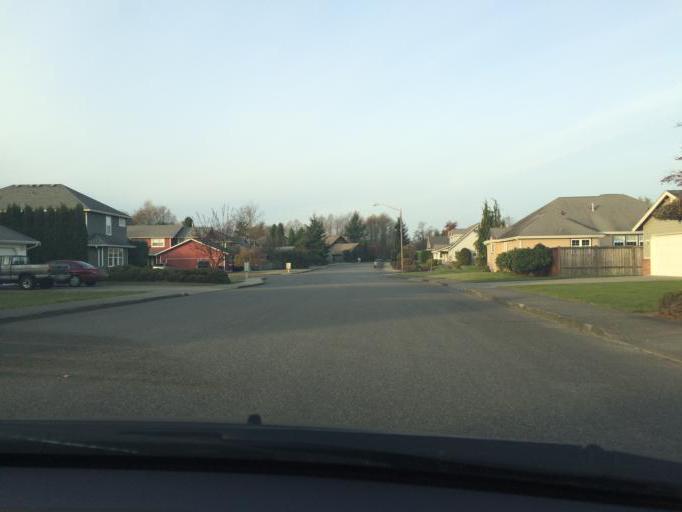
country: US
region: Washington
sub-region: Whatcom County
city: Lynden
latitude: 48.9566
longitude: -122.4337
